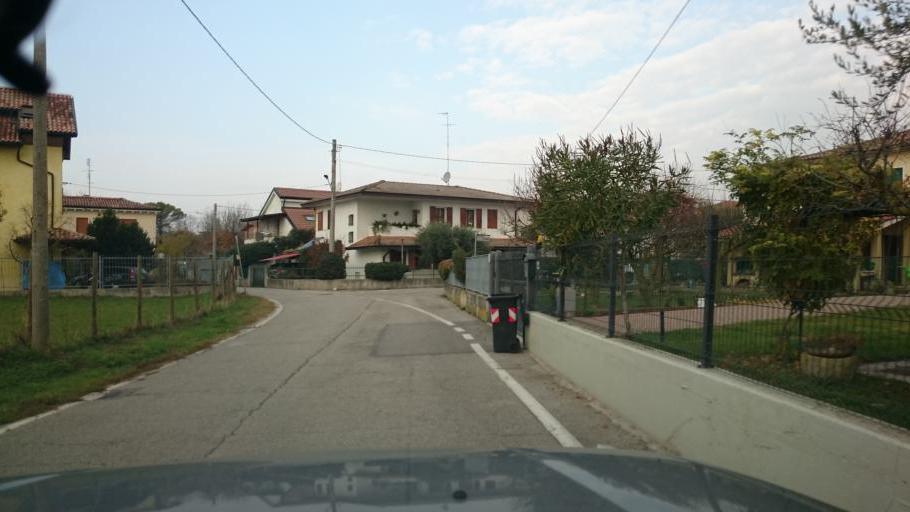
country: IT
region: Veneto
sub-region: Provincia di Padova
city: Tencarola
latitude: 45.3932
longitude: 11.8289
